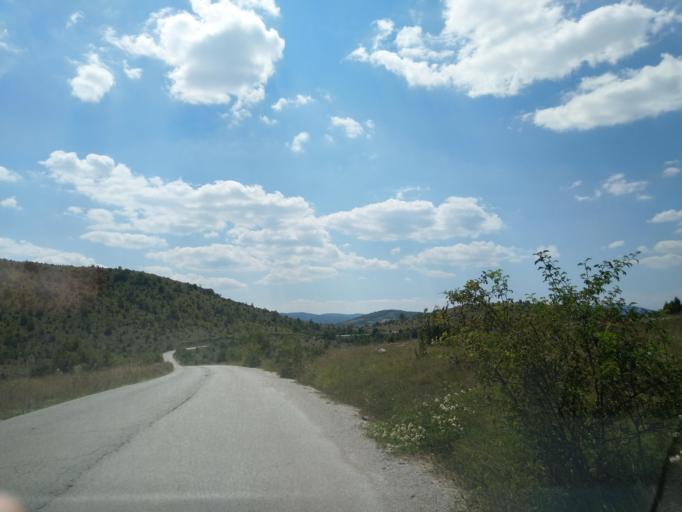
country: RS
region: Central Serbia
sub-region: Zlatiborski Okrug
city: Nova Varos
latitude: 43.4294
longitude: 19.9483
